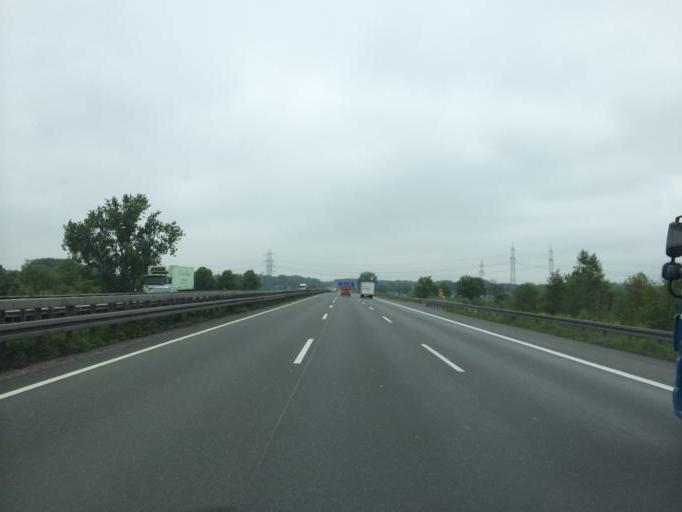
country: DE
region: North Rhine-Westphalia
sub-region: Regierungsbezirk Arnsberg
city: Welver
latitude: 51.6867
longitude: 7.9600
